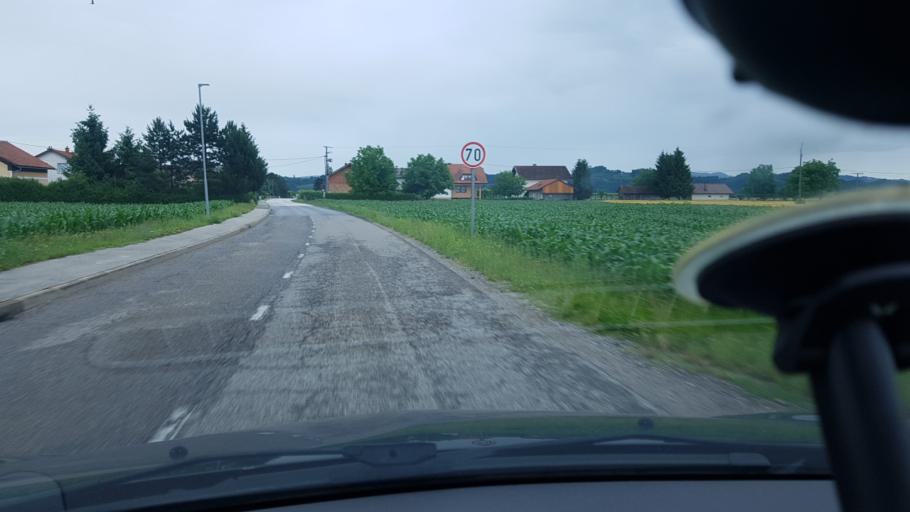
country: SI
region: Ptuj
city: Ptuj
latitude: 46.3860
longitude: 15.8744
